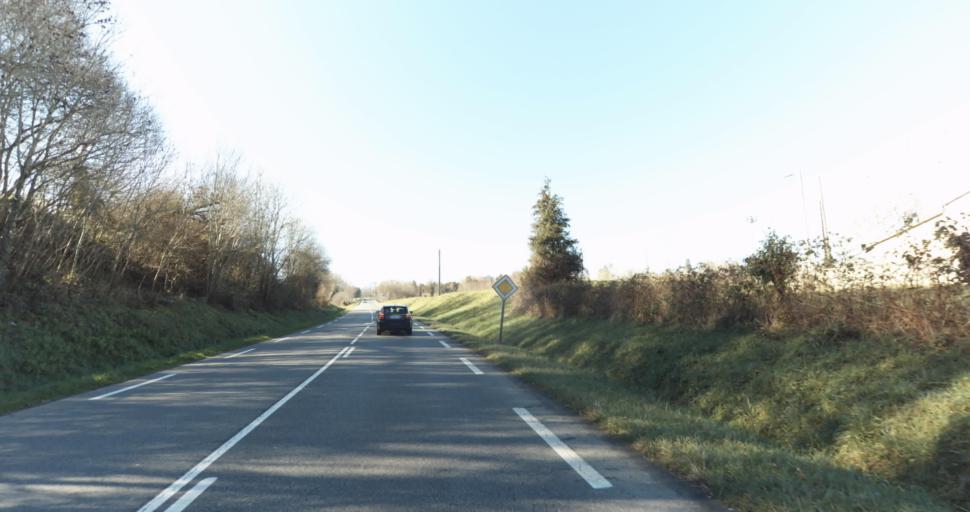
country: FR
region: Aquitaine
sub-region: Departement des Pyrenees-Atlantiques
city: Morlaas
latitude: 43.3383
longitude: -0.2640
